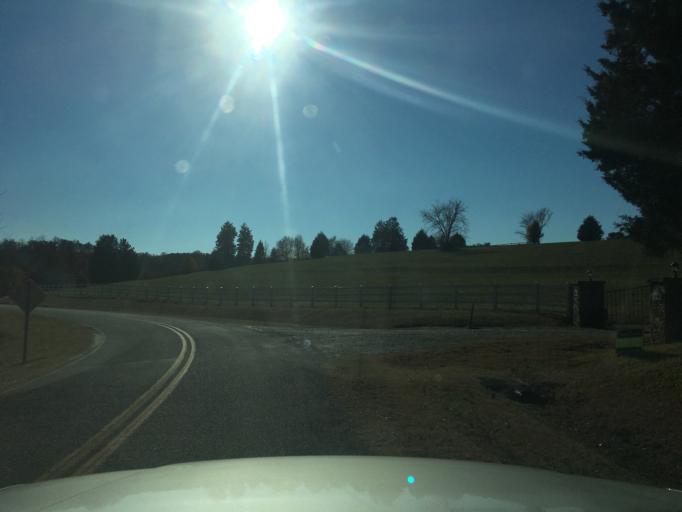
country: US
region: North Carolina
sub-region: Rutherford County
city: Rutherfordton
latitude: 35.2596
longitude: -82.0337
